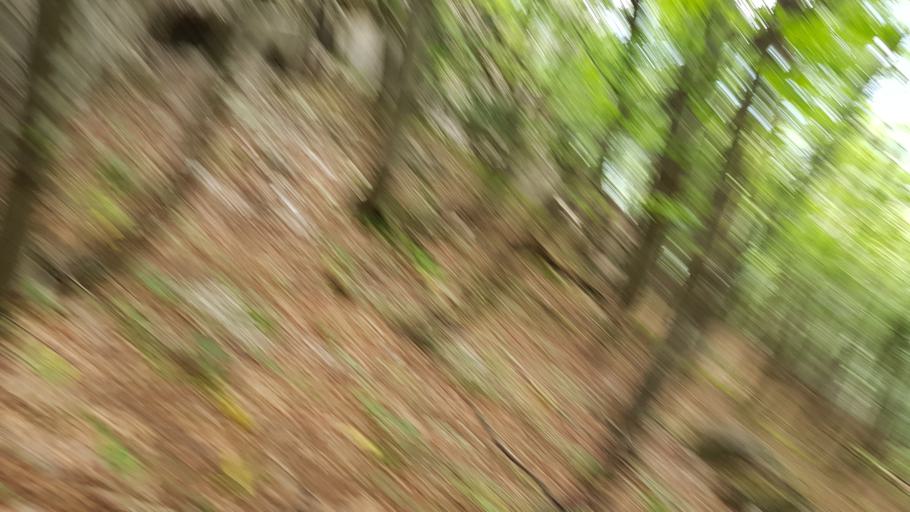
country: SI
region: Bovec
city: Bovec
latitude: 46.4169
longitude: 13.5728
